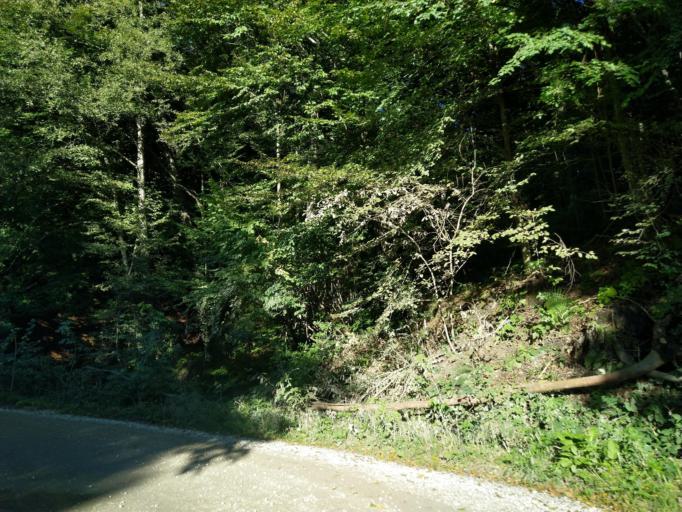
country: RS
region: Central Serbia
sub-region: Moravicki Okrug
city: Ivanjica
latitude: 43.4792
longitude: 20.2399
